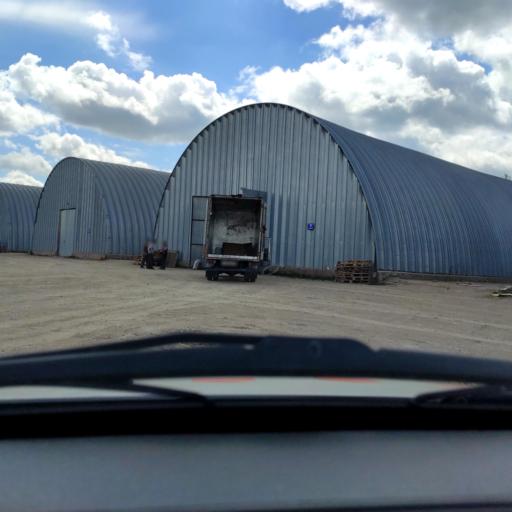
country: RU
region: Bashkortostan
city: Mikhaylovka
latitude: 54.8026
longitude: 55.8509
